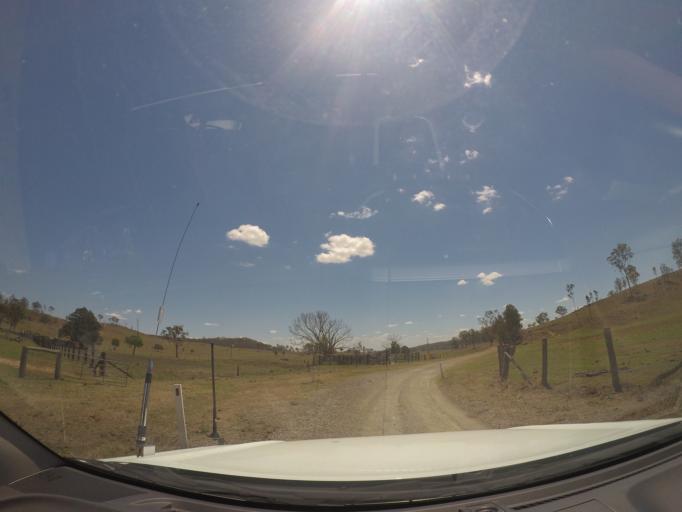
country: AU
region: Queensland
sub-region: Ipswich
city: Redbank Plains
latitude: -27.7470
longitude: 152.8301
